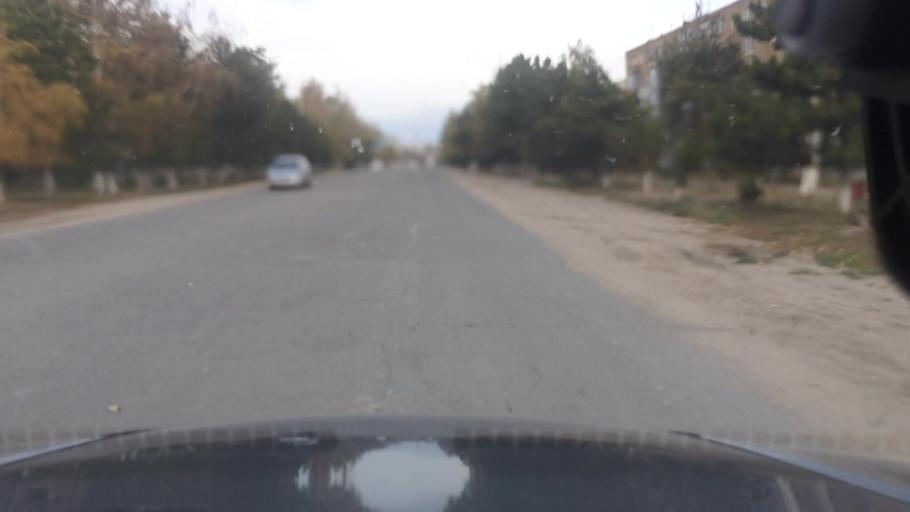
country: KG
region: Ysyk-Koel
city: Karakol
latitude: 42.4970
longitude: 78.3905
